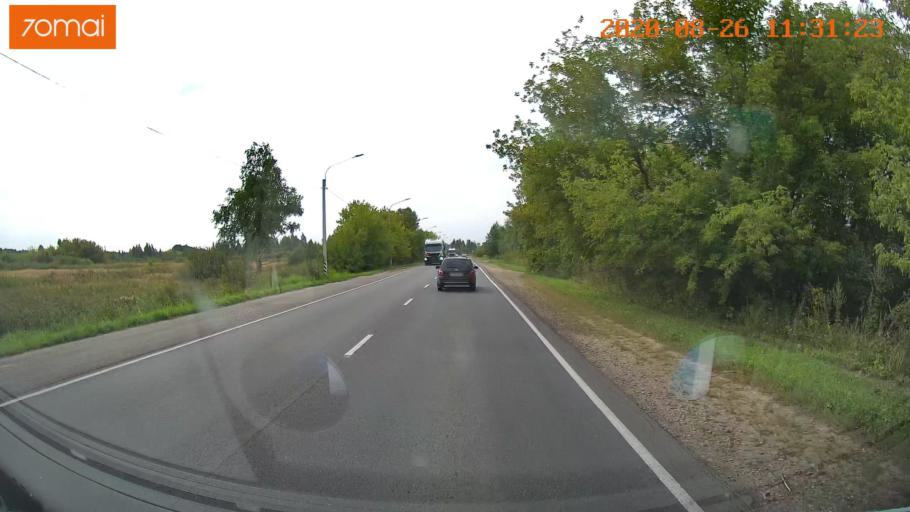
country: RU
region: Rjazan
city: Shilovo
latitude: 54.3067
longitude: 40.8743
